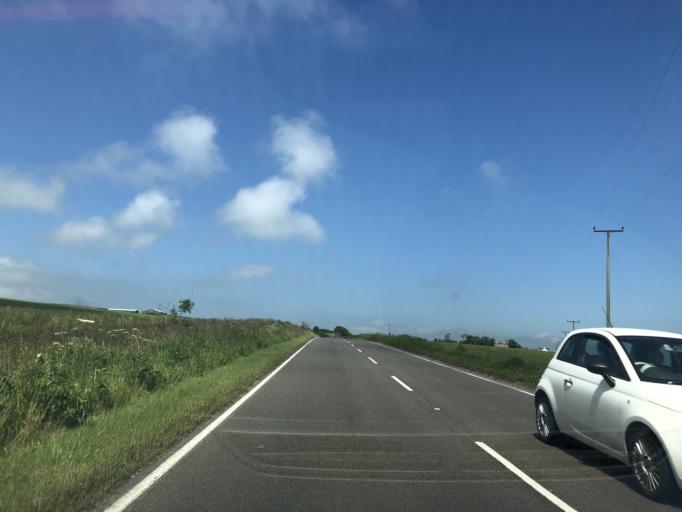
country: GB
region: Scotland
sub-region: Aberdeenshire
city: Stonehaven
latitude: 56.9282
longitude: -2.2063
